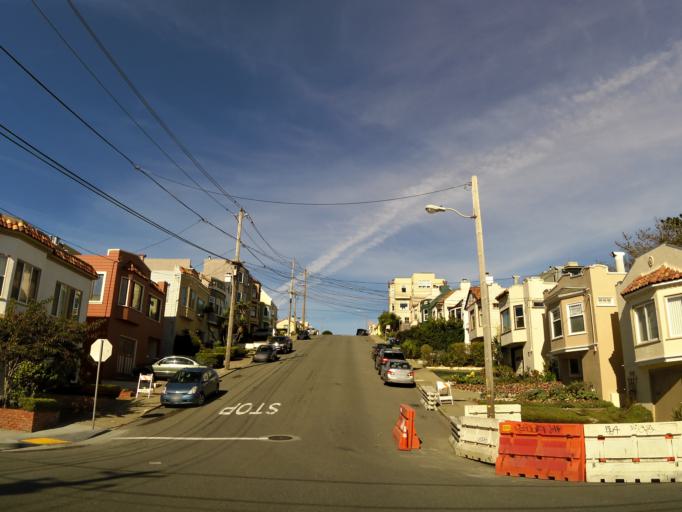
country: US
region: California
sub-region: San Mateo County
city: Daly City
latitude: 37.7761
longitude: -122.5081
